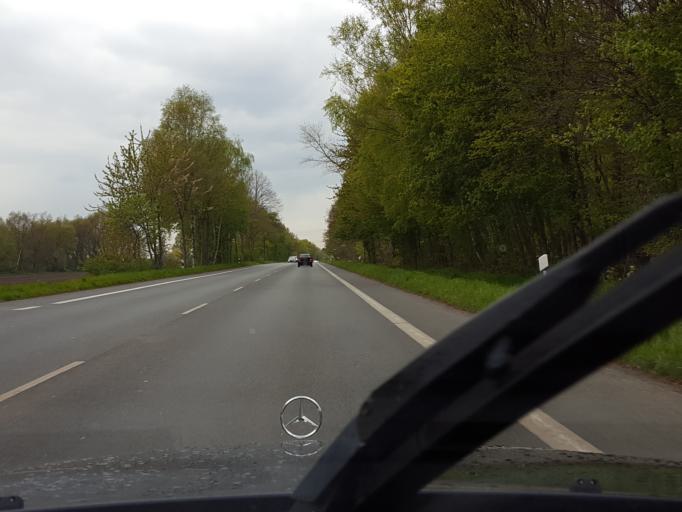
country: DE
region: North Rhine-Westphalia
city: Waltrop
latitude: 51.6209
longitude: 7.3771
